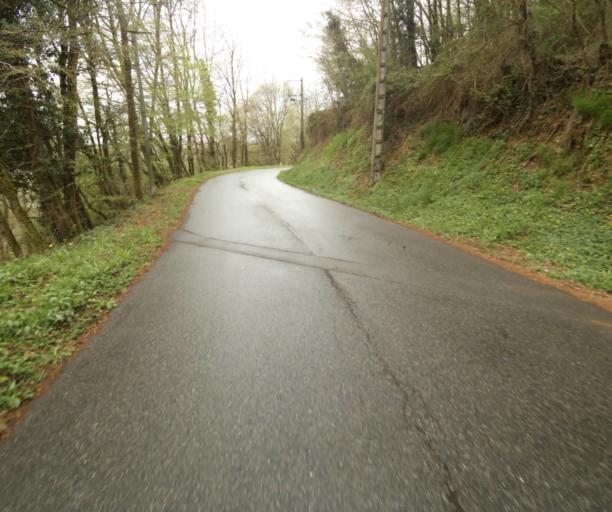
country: FR
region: Limousin
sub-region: Departement de la Correze
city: Tulle
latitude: 45.2687
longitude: 1.7615
